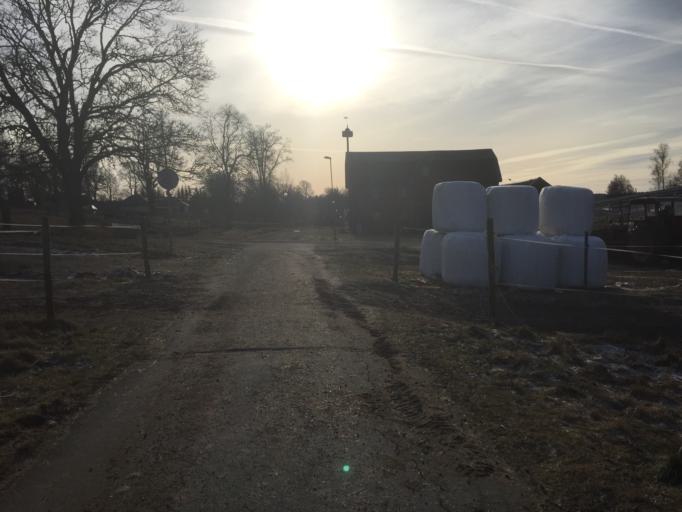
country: SE
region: Joenkoeping
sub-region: Aneby Kommun
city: Aneby
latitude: 57.8265
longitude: 14.8155
